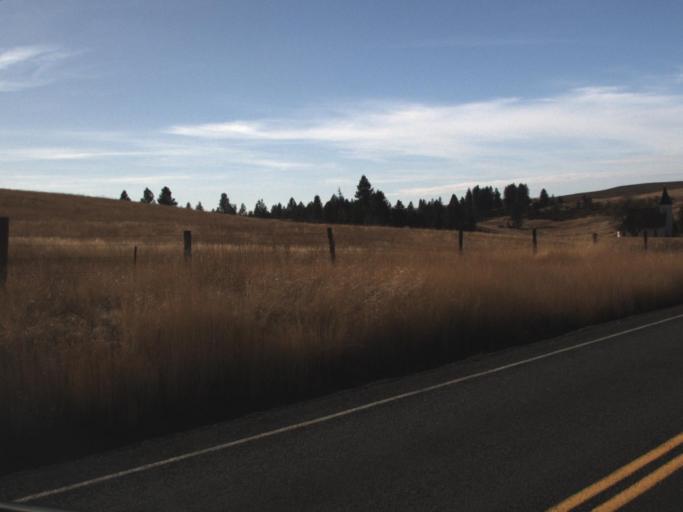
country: US
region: Washington
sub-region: Lincoln County
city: Davenport
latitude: 47.8615
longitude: -118.2258
